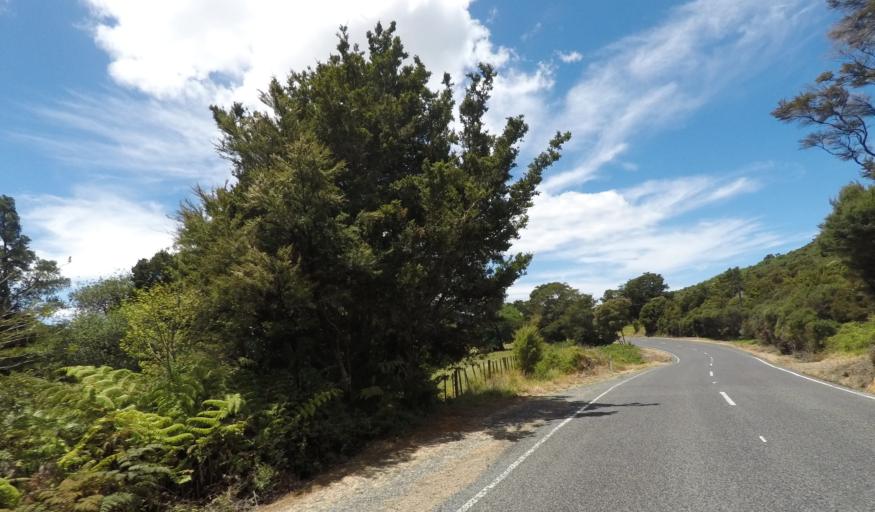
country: NZ
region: Northland
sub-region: Whangarei
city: Ngunguru
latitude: -35.5077
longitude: 174.4197
